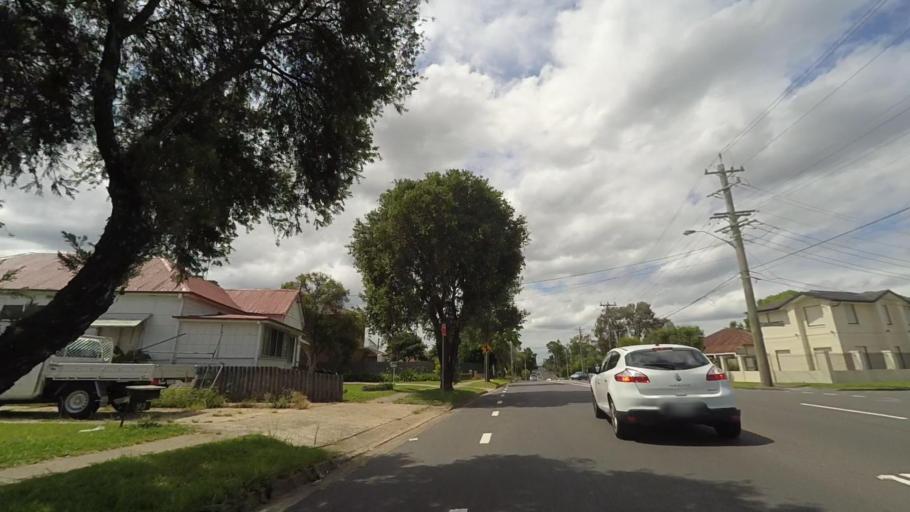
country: AU
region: New South Wales
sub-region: Fairfield
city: Fairfield Heights
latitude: -33.8710
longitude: 150.9466
